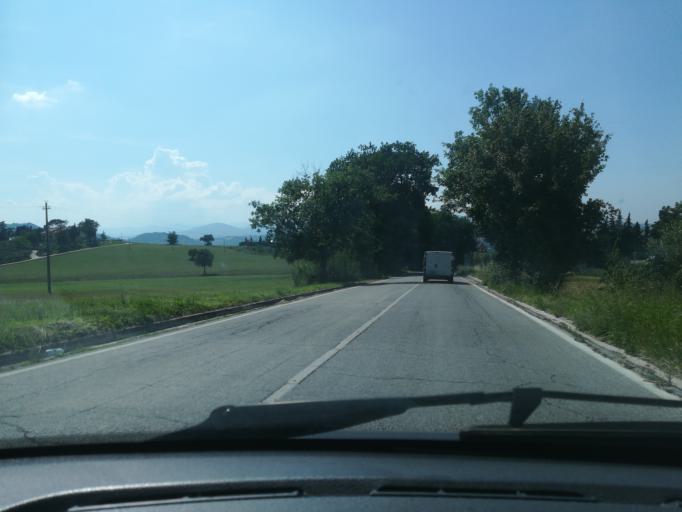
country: IT
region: The Marches
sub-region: Provincia di Macerata
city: Casette Verdini
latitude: 43.2859
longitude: 13.3938
